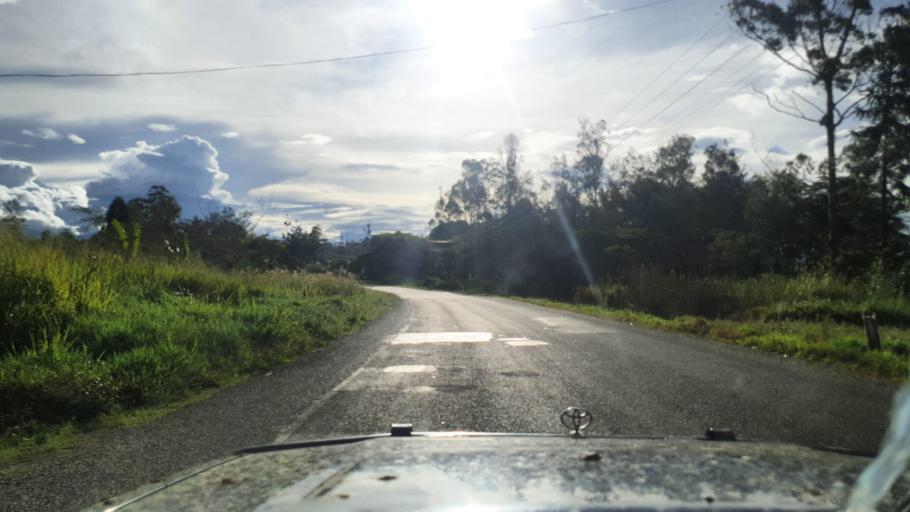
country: PG
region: Jiwaka
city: Minj
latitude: -5.8753
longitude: 144.7144
